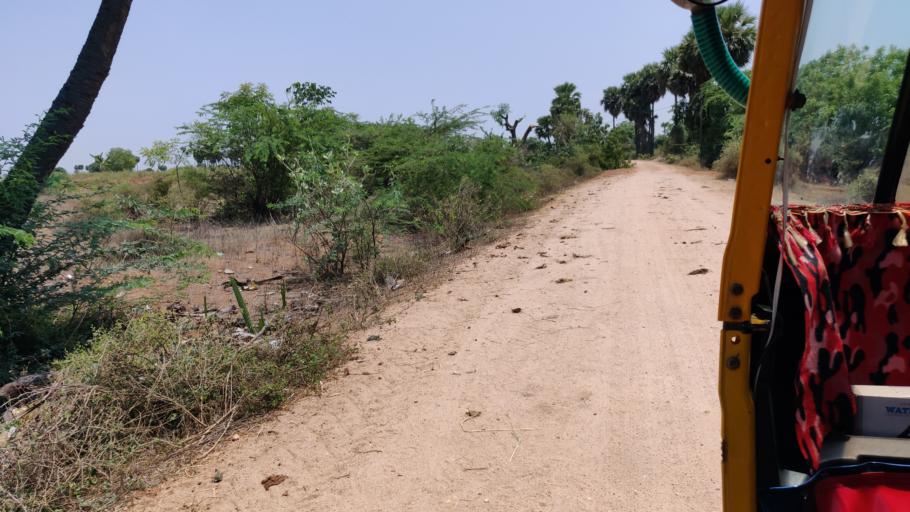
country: IN
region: Telangana
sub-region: Nalgonda
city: Mirialguda
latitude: 17.0118
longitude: 79.5459
